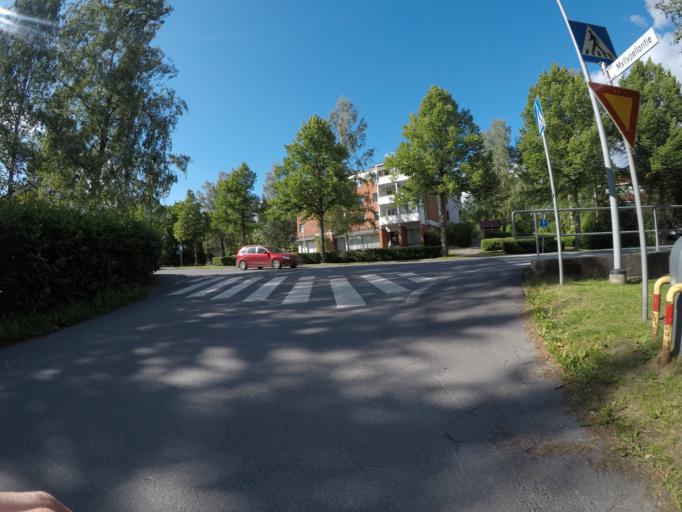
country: FI
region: Haeme
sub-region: Haemeenlinna
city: Haemeenlinna
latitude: 61.0031
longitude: 24.4937
